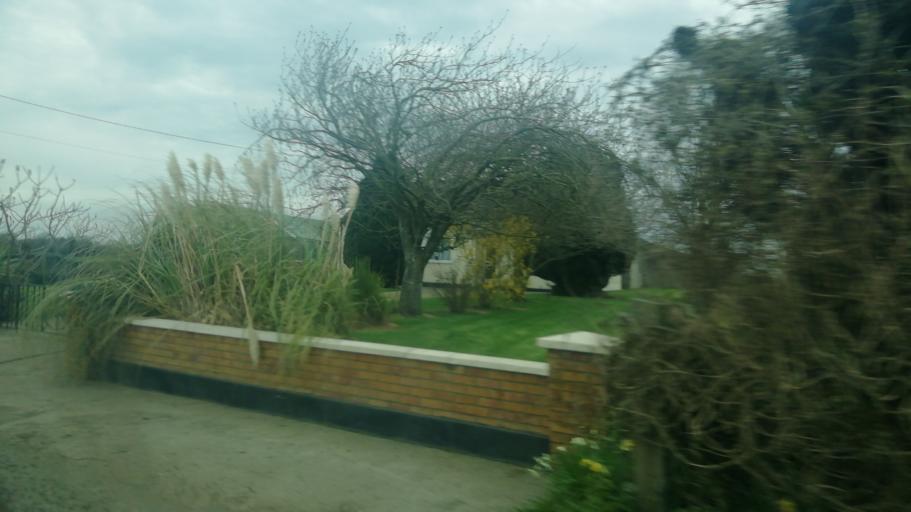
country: IE
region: Leinster
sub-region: Kildare
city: Maynooth
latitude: 53.3536
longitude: -6.6143
